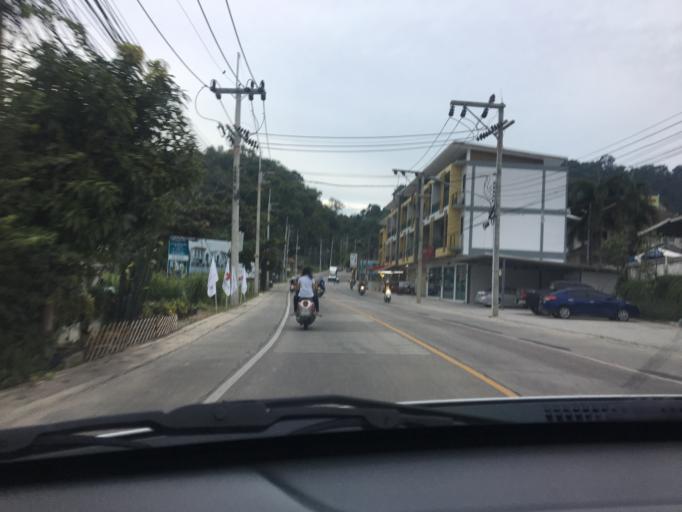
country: TH
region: Phuket
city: Ban Ratsada
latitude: 7.9062
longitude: 98.4031
